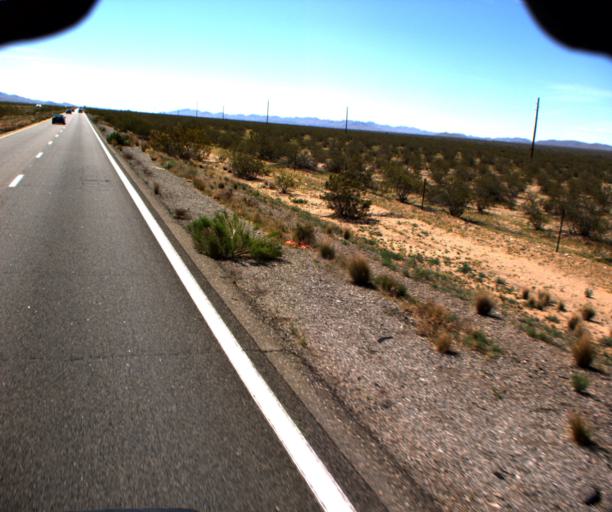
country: US
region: Arizona
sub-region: Mohave County
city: Dolan Springs
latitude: 35.5886
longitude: -114.3935
